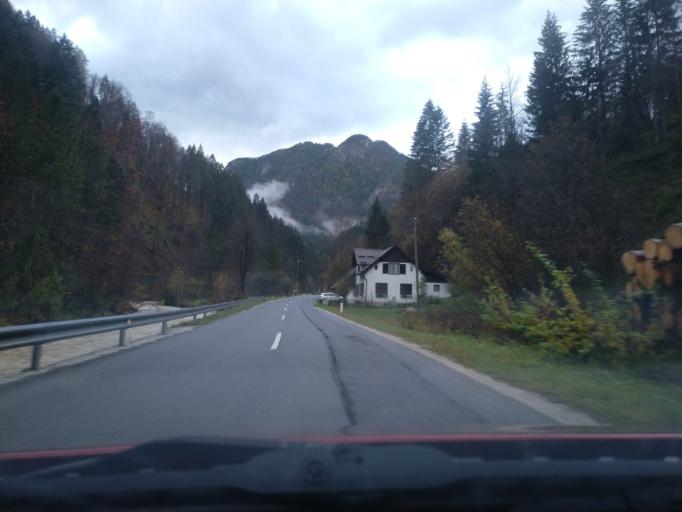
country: SI
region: Solcava
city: Solcava
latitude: 46.4158
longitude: 14.7004
